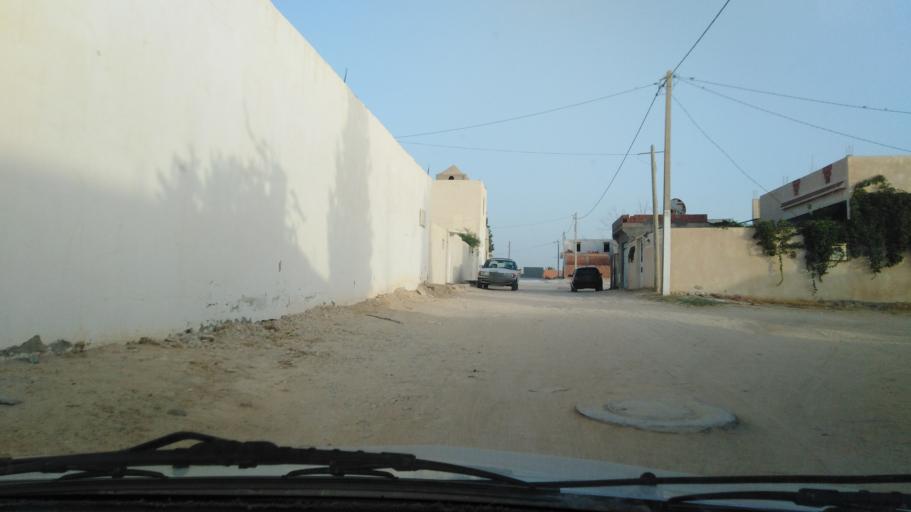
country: TN
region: Qabis
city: Gabes
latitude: 33.9528
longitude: 9.9956
